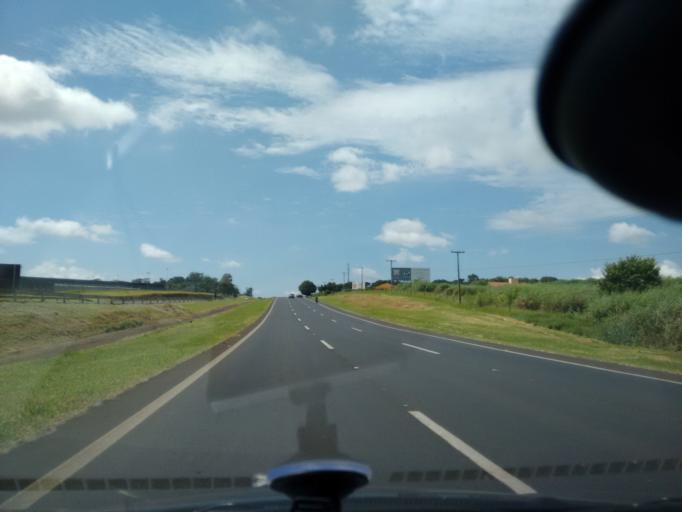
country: BR
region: Sao Paulo
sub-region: Ibate
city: Ibate
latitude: -21.9726
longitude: -47.9449
